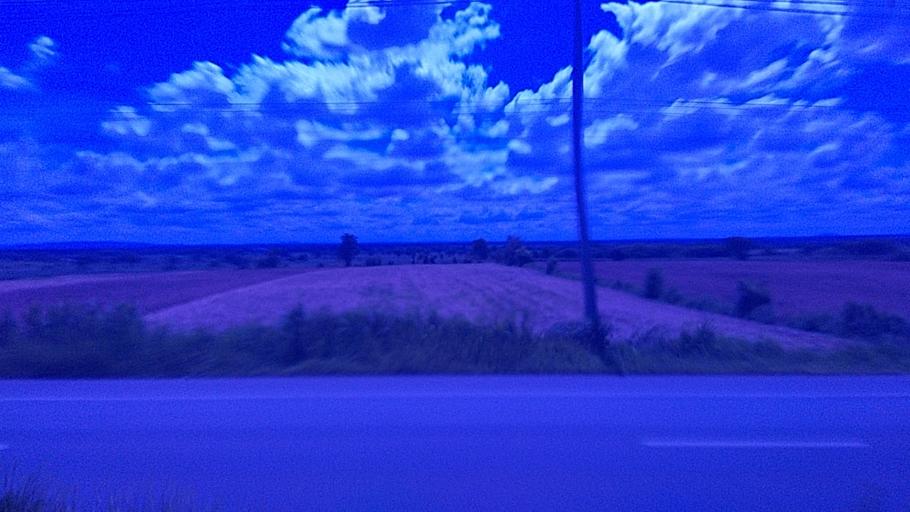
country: TH
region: Nakhon Ratchasima
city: Dan Khun Thot
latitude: 15.1349
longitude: 101.7286
